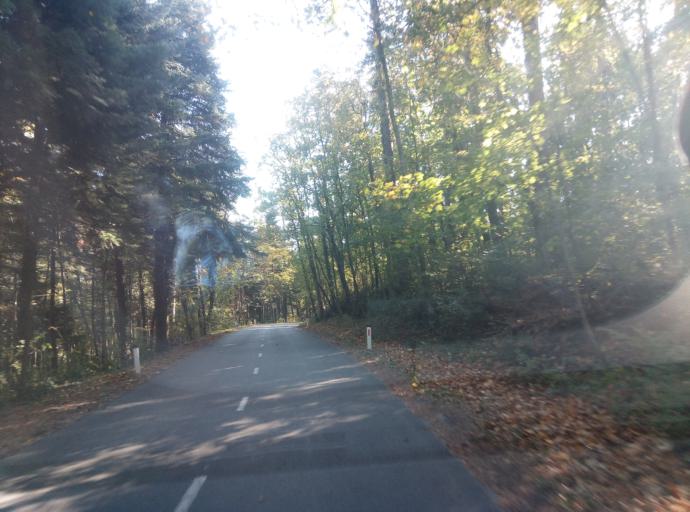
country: SI
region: Komen
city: Komen
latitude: 45.8197
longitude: 13.7482
